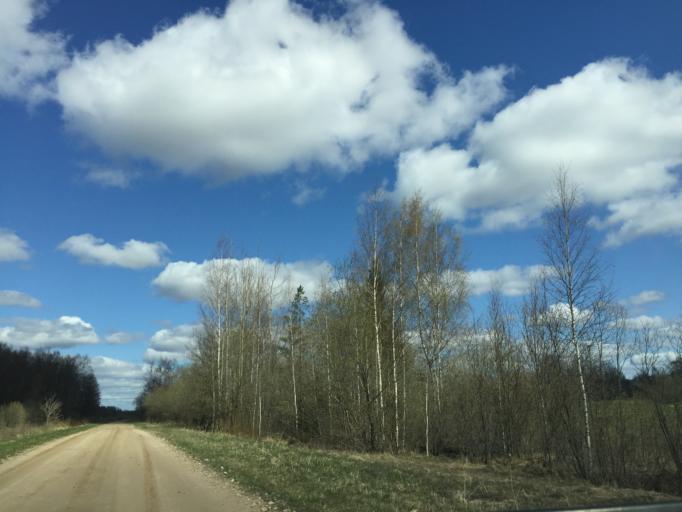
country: LV
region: Vilanu
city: Vilani
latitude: 56.6774
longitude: 27.0950
